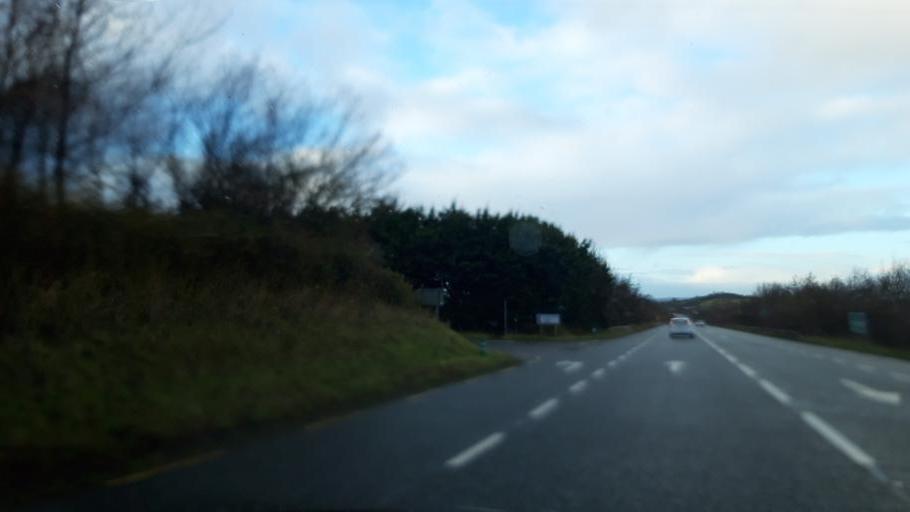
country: IE
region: Leinster
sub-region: Lu
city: Ardee
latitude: 53.9149
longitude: -6.6250
